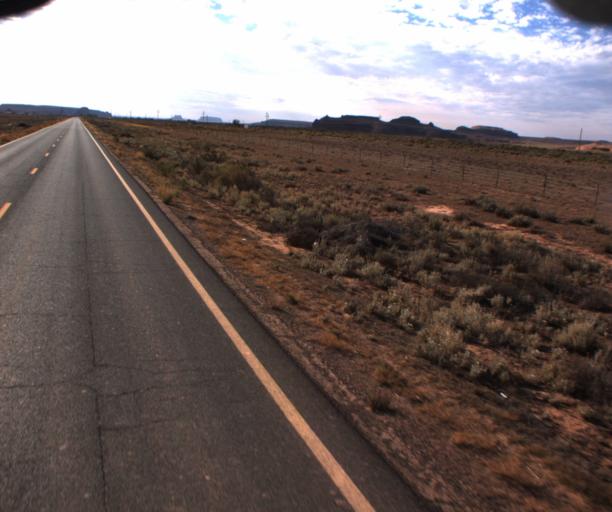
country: US
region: Arizona
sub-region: Apache County
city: Many Farms
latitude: 36.7469
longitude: -109.6409
